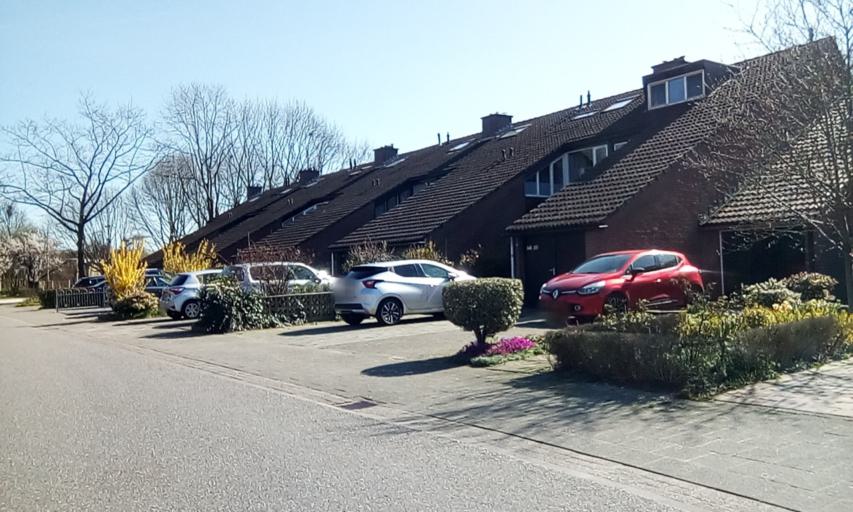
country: NL
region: Gelderland
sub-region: Gemeente Nijmegen
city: Lindenholt
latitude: 51.8015
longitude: 5.8080
